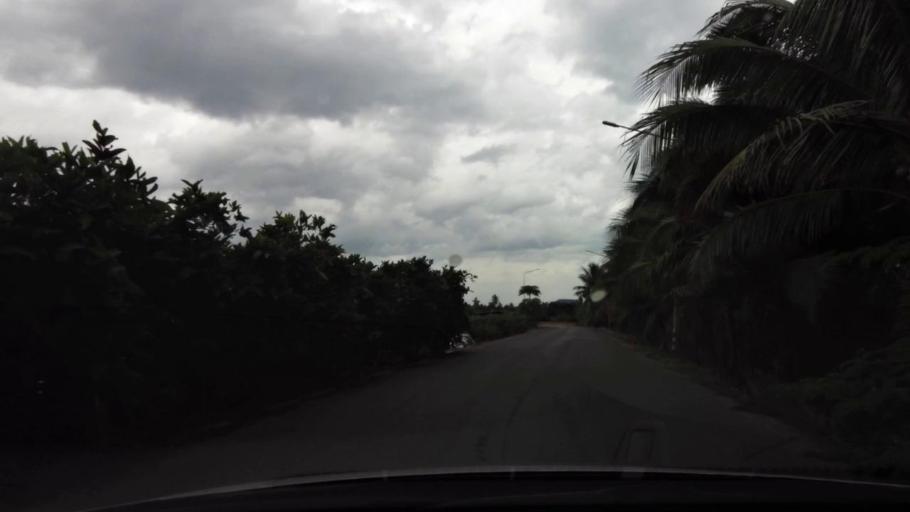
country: TH
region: Ratchaburi
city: Damnoen Saduak
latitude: 13.5746
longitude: 99.9806
